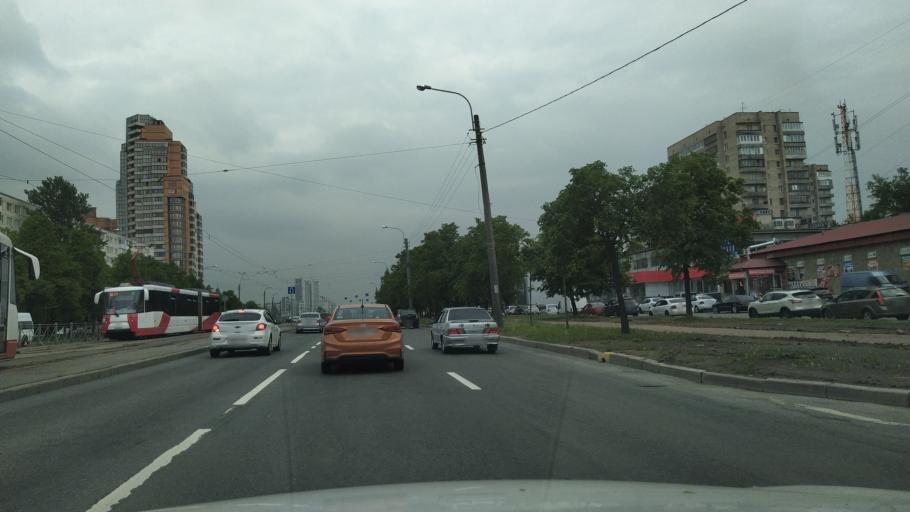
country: RU
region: St.-Petersburg
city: Kupchino
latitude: 59.8618
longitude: 30.3894
